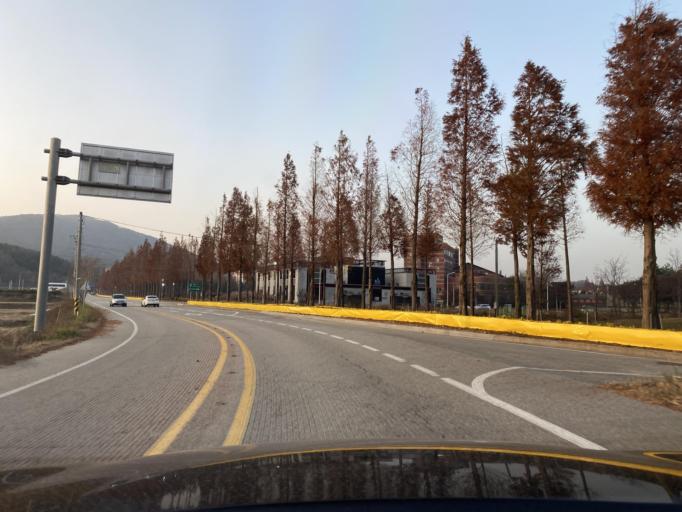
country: KR
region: Chungcheongnam-do
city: Hongsung
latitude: 36.6868
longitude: 126.6598
